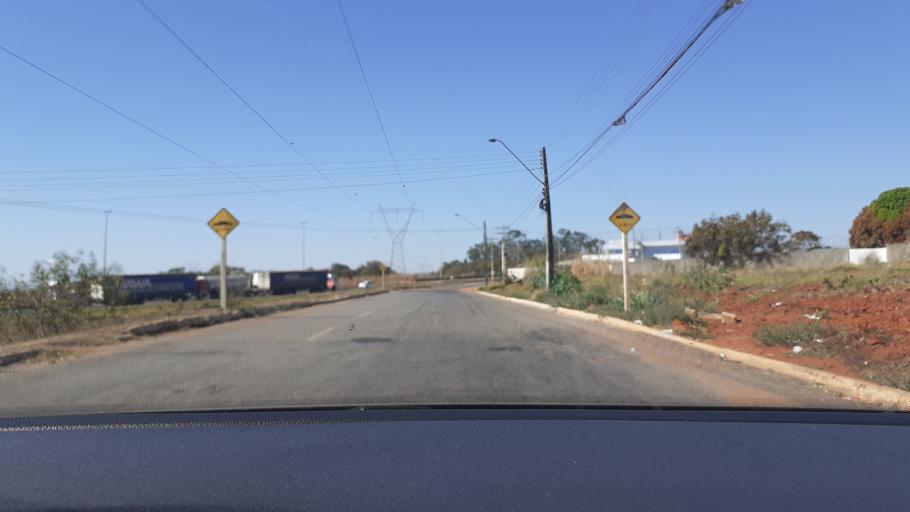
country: BR
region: Goias
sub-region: Aparecida De Goiania
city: Aparecida de Goiania
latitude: -16.8344
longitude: -49.2449
